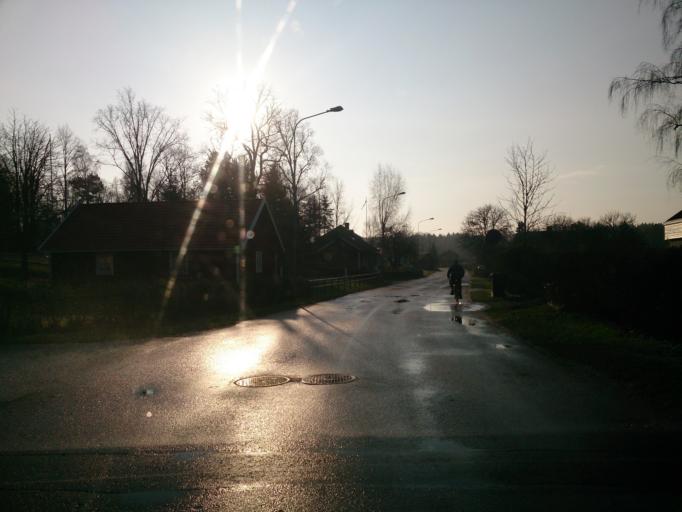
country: SE
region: OEstergoetland
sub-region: Atvidabergs Kommun
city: Atvidaberg
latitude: 58.3348
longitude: 16.0234
